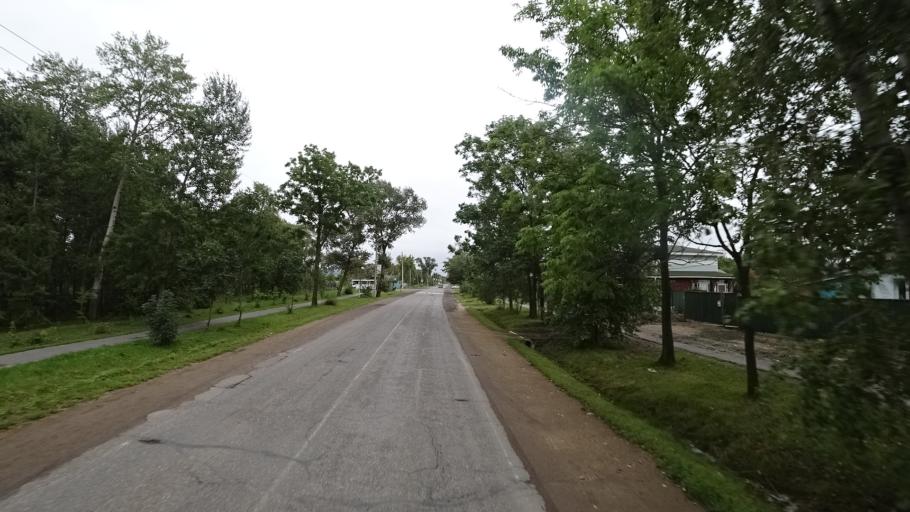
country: RU
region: Primorskiy
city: Chernigovka
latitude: 44.3401
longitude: 132.5806
